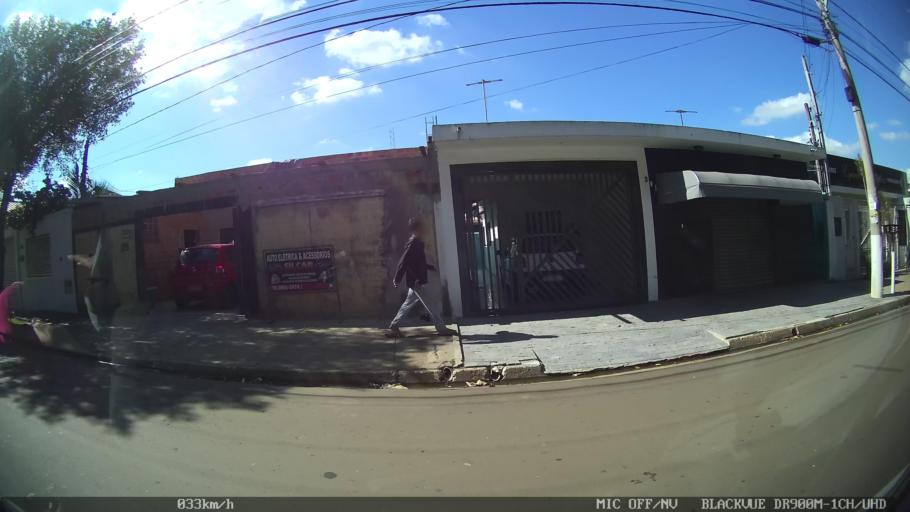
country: BR
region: Sao Paulo
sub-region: Hortolandia
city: Hortolandia
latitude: -22.8924
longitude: -47.2211
